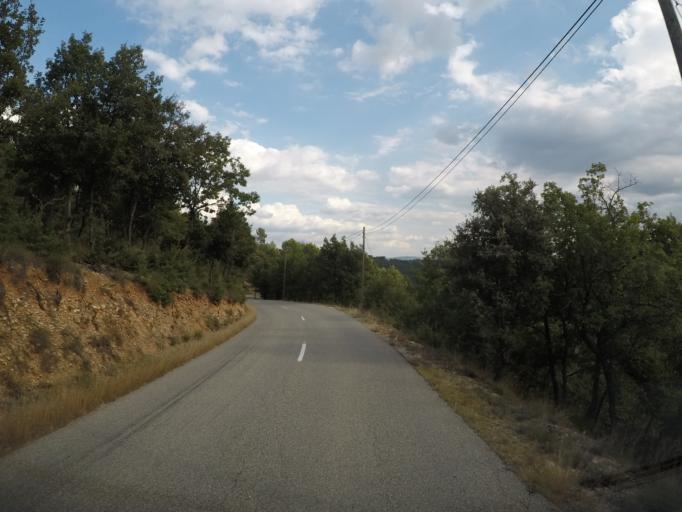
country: FR
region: Provence-Alpes-Cote d'Azur
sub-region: Departement des Alpes-de-Haute-Provence
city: Riez
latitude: 43.8217
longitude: 6.0480
